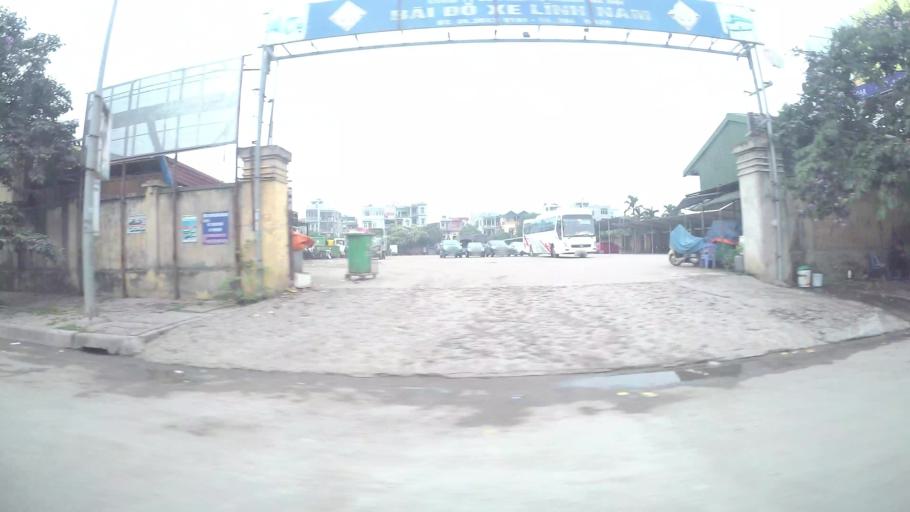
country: VN
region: Ha Noi
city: Hai BaTrung
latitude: 20.9825
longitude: 105.8912
